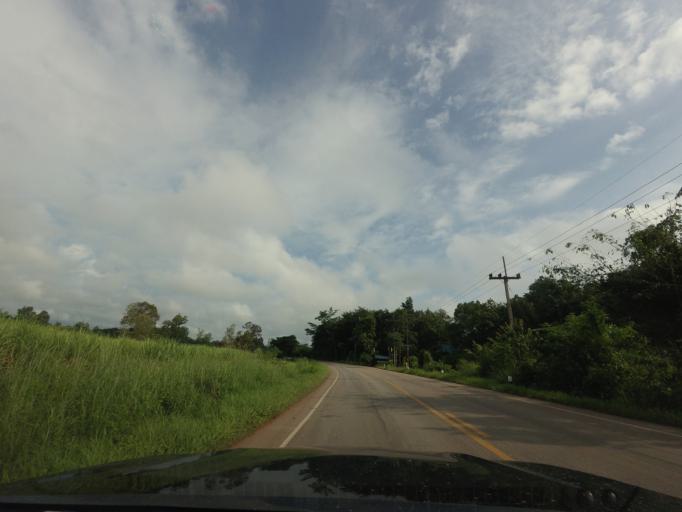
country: TH
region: Changwat Udon Thani
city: Nam Som
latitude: 17.8558
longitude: 102.2573
